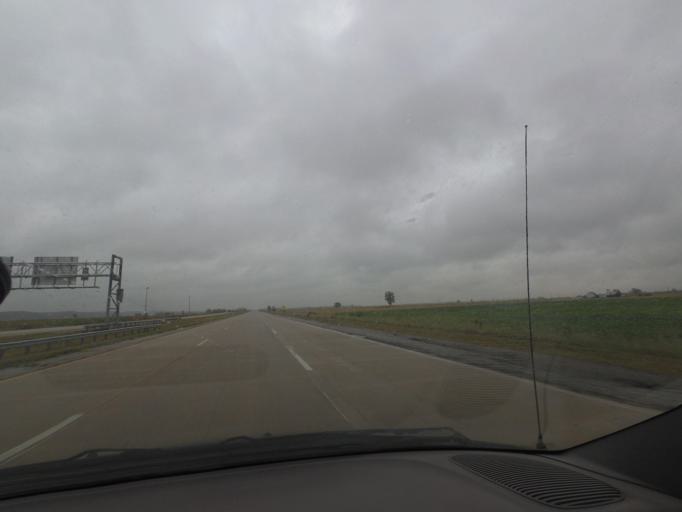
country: US
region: Illinois
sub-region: Adams County
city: Payson
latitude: 39.7500
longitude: -91.2868
